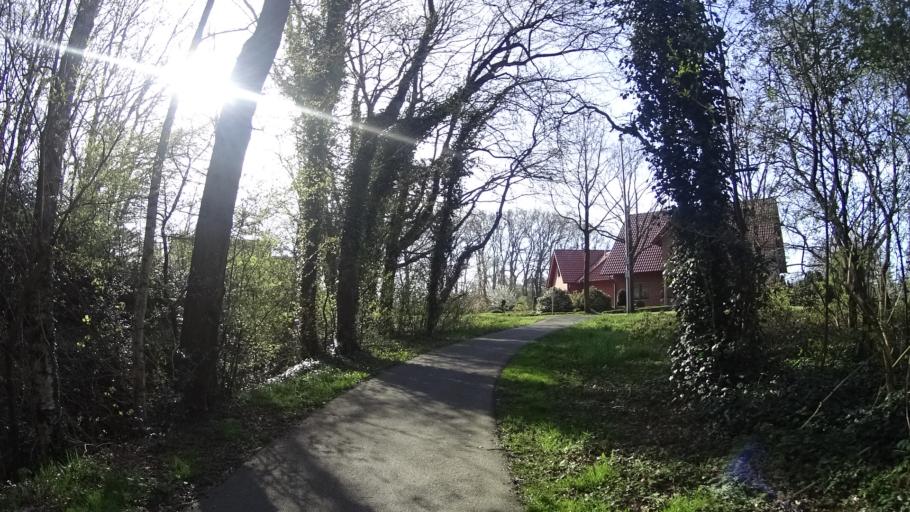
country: DE
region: Lower Saxony
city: Haren
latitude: 52.7908
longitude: 7.2760
